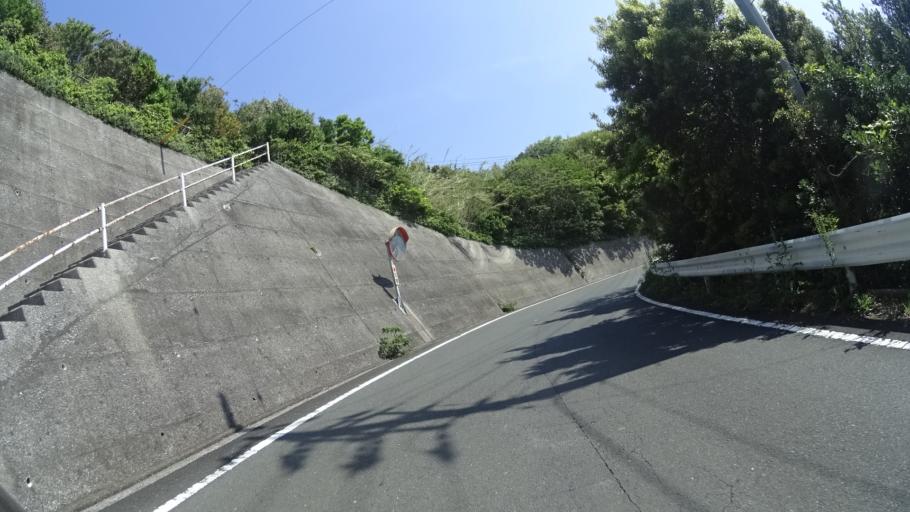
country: JP
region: Ehime
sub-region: Nishiuwa-gun
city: Ikata-cho
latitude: 33.3678
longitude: 132.0482
